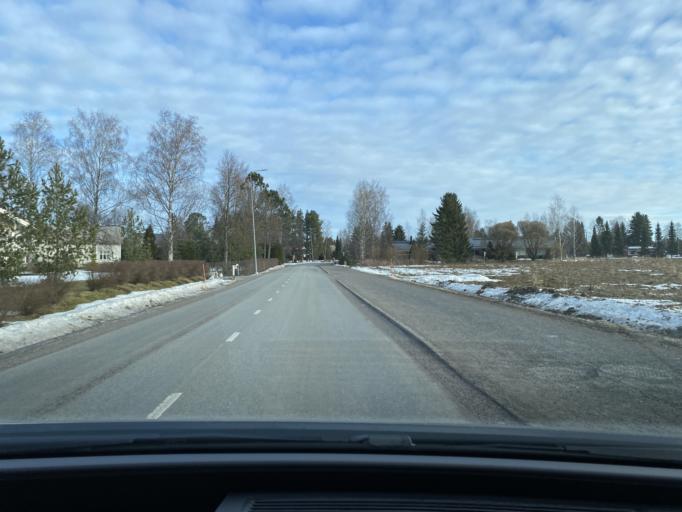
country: FI
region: Satakunta
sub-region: Pori
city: Huittinen
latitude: 61.1695
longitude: 22.6924
